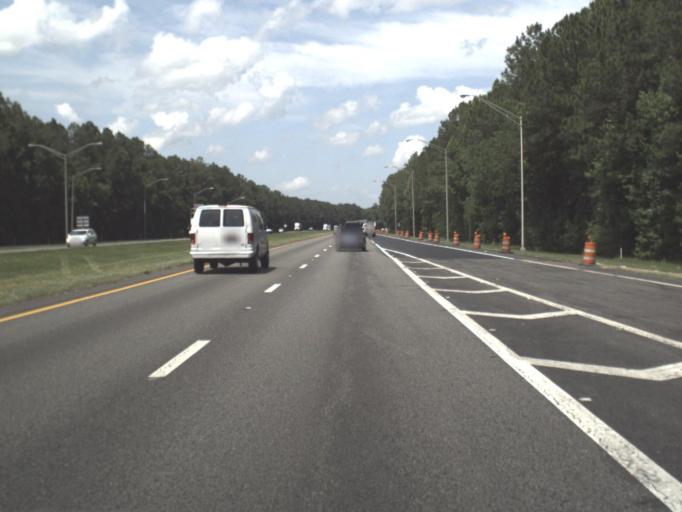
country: US
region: Florida
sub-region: Nassau County
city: Nassau Village-Ratliff
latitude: 30.4421
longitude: -81.7219
